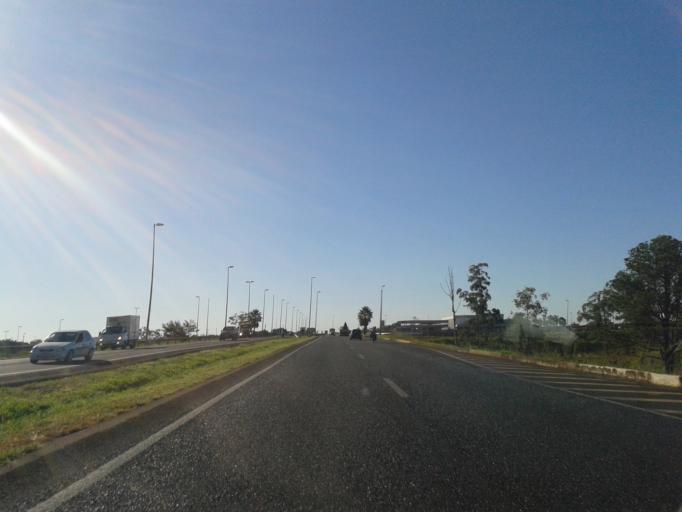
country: BR
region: Minas Gerais
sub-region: Uberlandia
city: Uberlandia
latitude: -18.9416
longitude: -48.2189
